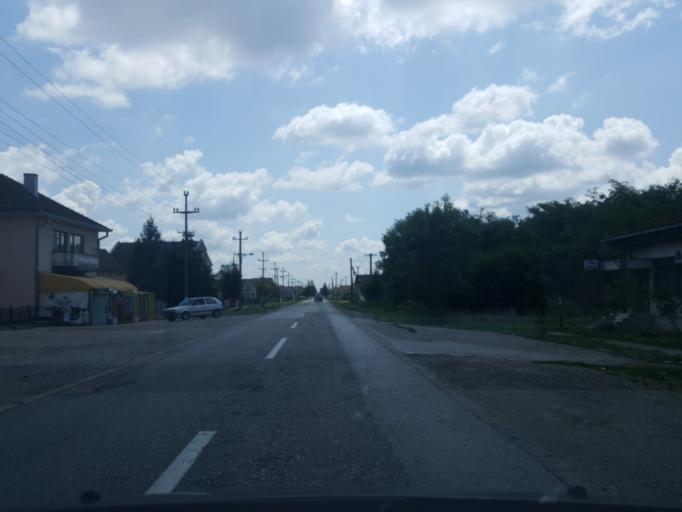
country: RS
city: Glusci
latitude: 44.8893
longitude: 19.5494
